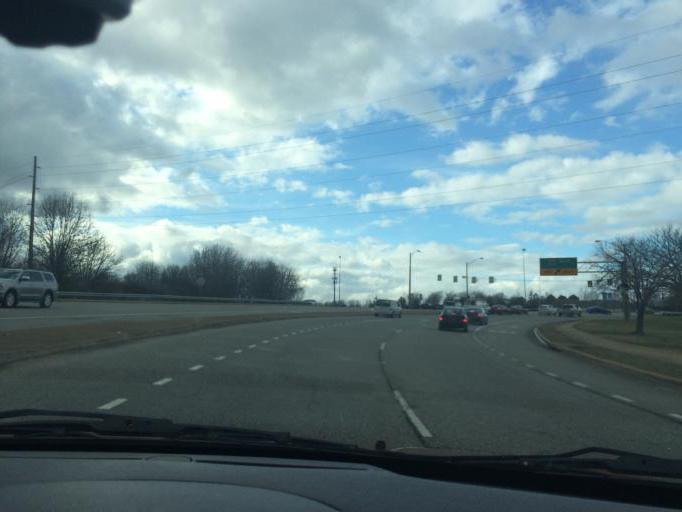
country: US
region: Alabama
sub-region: Madison County
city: Redstone Arsenal
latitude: 34.7133
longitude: -86.6424
